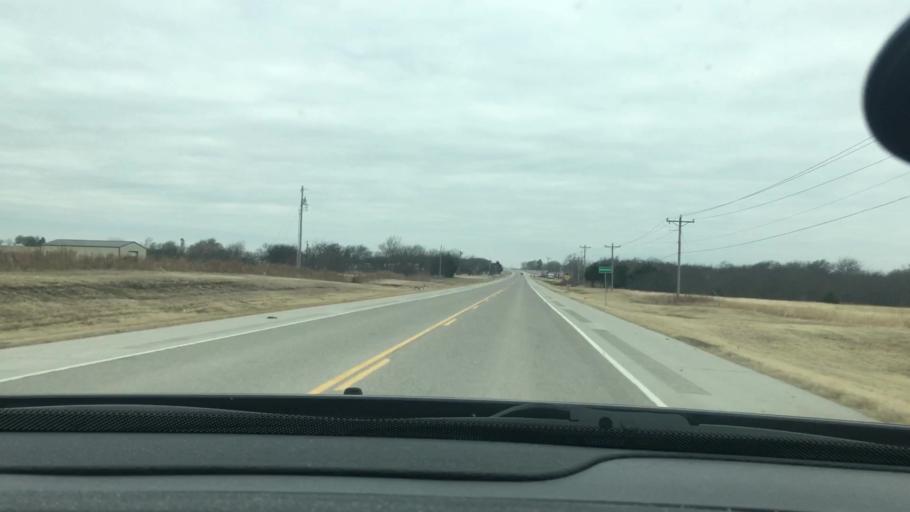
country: US
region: Oklahoma
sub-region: Garvin County
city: Wynnewood
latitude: 34.5110
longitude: -97.3418
